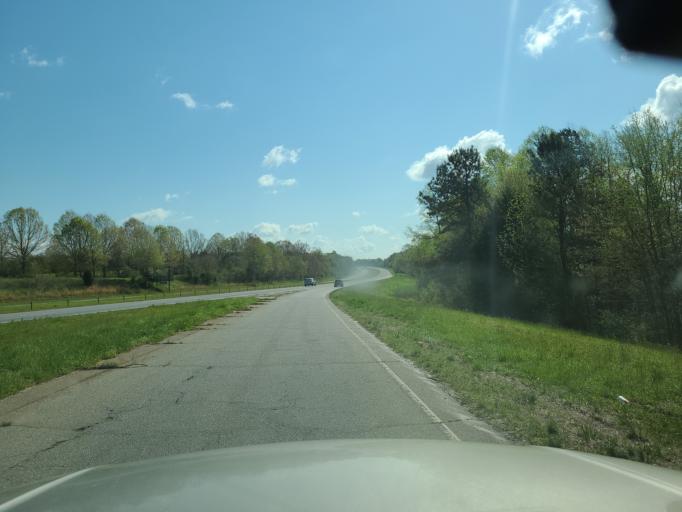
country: US
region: North Carolina
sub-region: Rutherford County
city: Spindale
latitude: 35.3070
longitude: -81.9186
